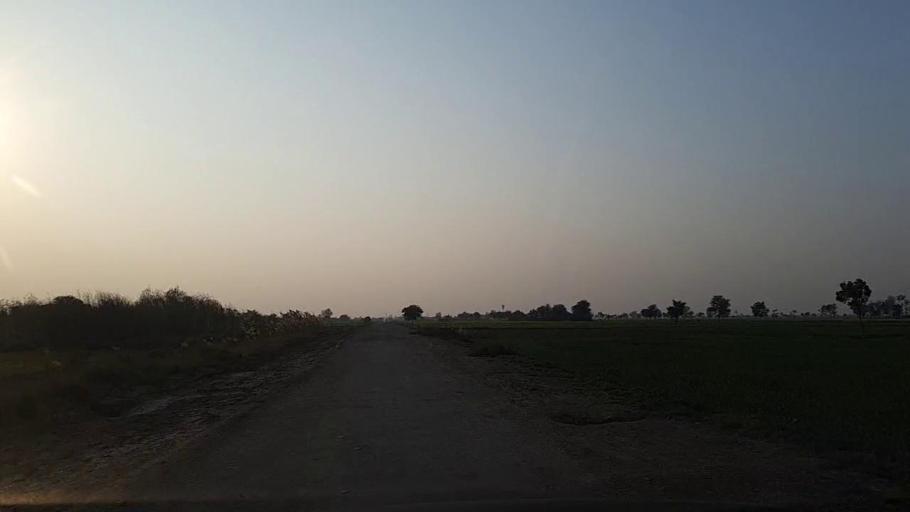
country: PK
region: Sindh
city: Daur
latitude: 26.4164
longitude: 68.3793
